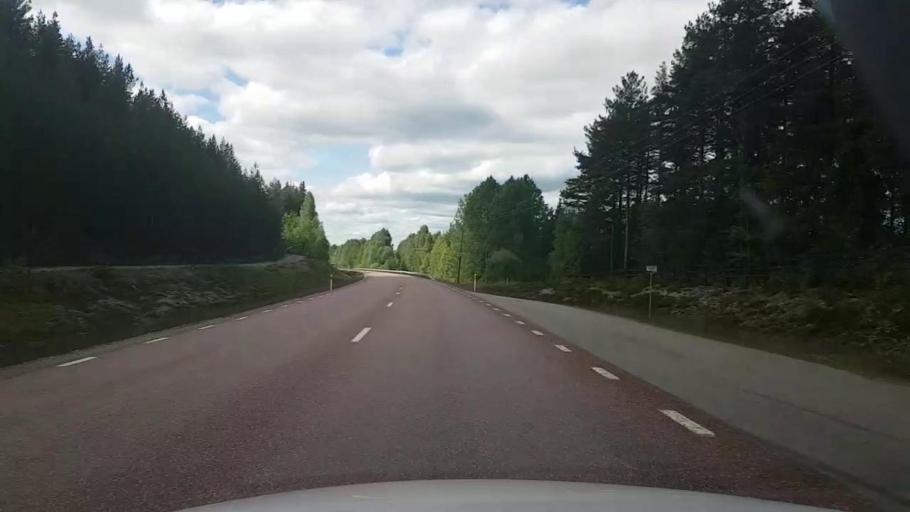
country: SE
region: Gaevleborg
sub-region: Ljusdals Kommun
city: Ljusdal
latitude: 61.8040
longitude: 16.1095
